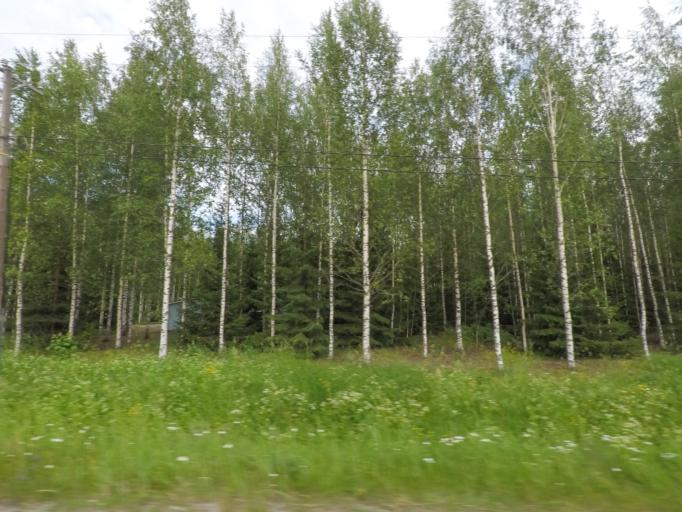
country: FI
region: Paijanne Tavastia
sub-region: Lahti
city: Hollola
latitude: 60.8808
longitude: 25.5060
